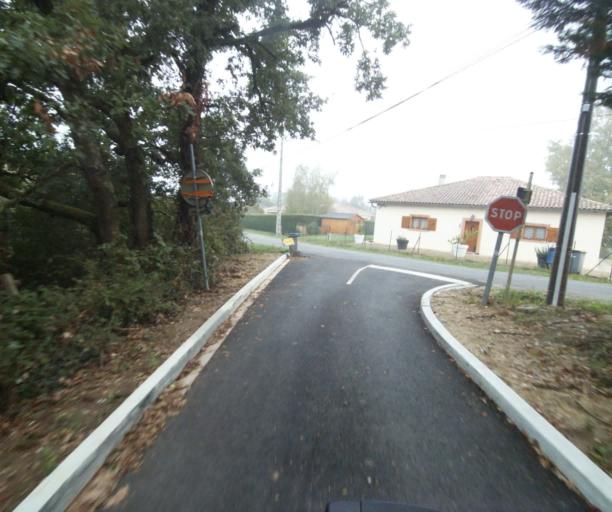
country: FR
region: Midi-Pyrenees
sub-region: Departement du Tarn-et-Garonne
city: Corbarieu
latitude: 43.9503
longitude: 1.3938
